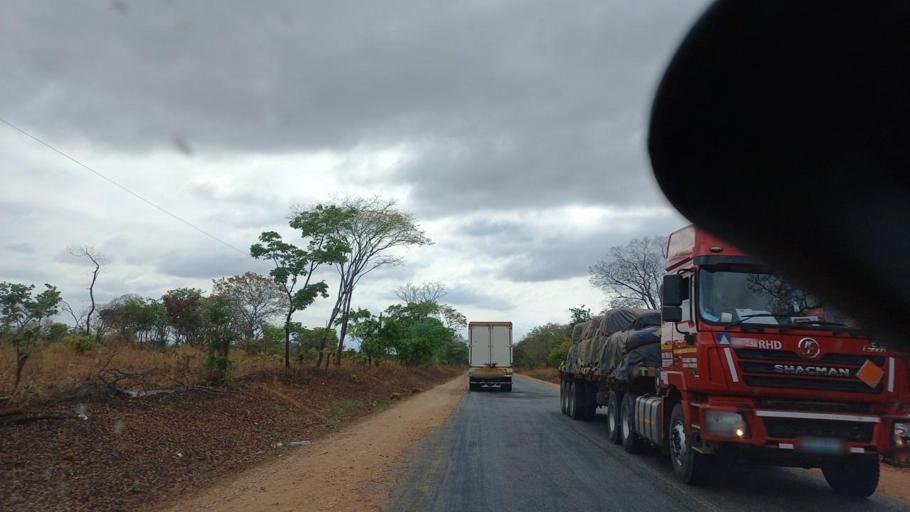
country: ZM
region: Lusaka
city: Chongwe
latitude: -15.1302
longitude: 29.5289
